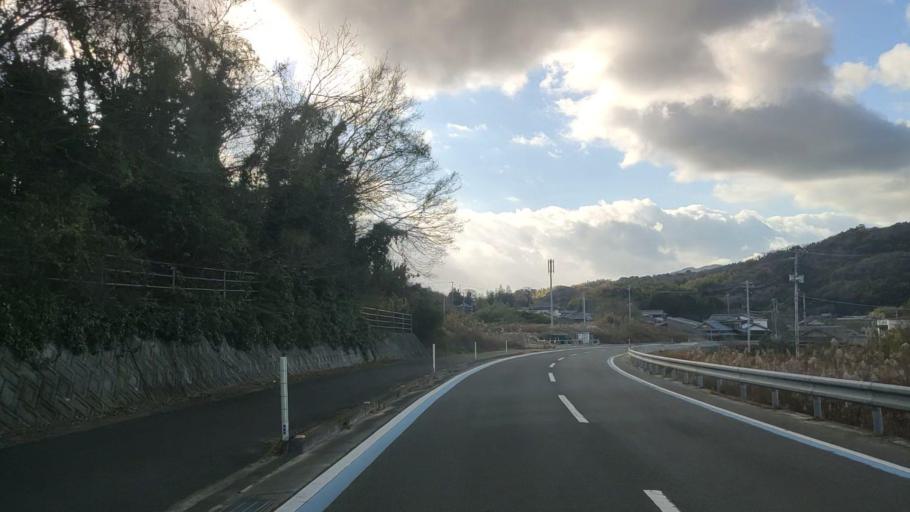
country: JP
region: Hiroshima
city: Innoshima
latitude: 34.2284
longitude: 133.0792
